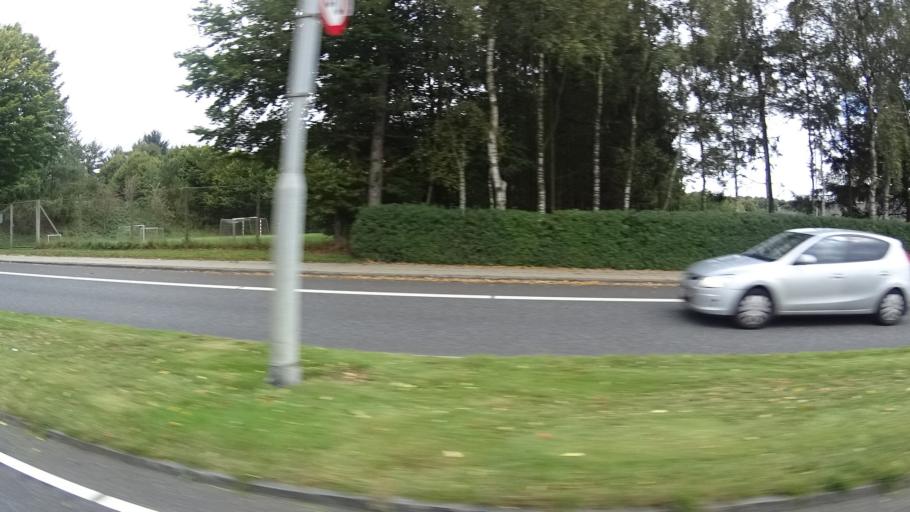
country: DK
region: South Denmark
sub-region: Vejle Kommune
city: Vejle
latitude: 55.6873
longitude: 9.5252
